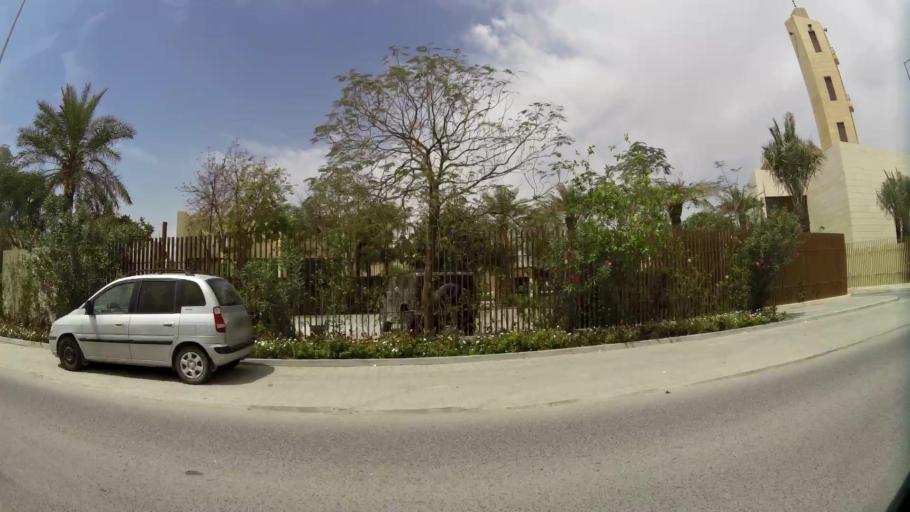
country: QA
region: Baladiyat ar Rayyan
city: Ar Rayyan
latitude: 25.2802
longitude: 51.4373
